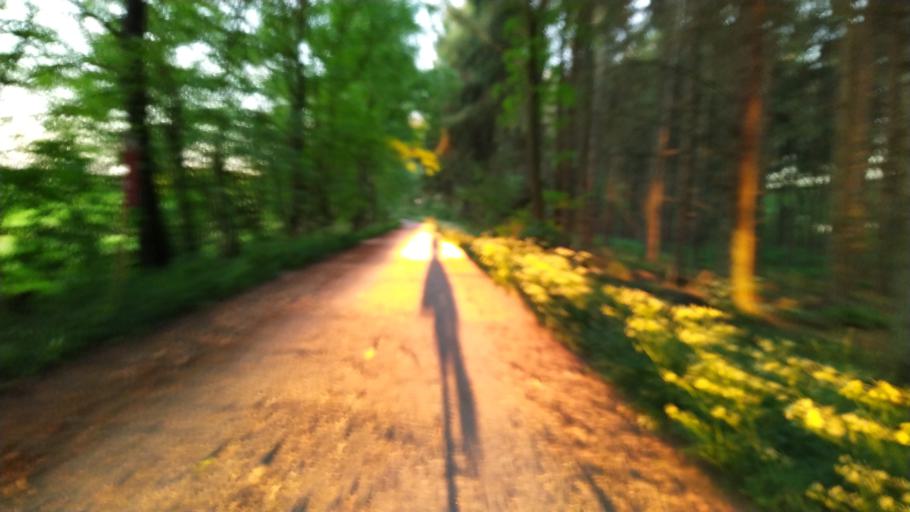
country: DE
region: Lower Saxony
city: Bargstedt
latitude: 53.4887
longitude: 9.4508
